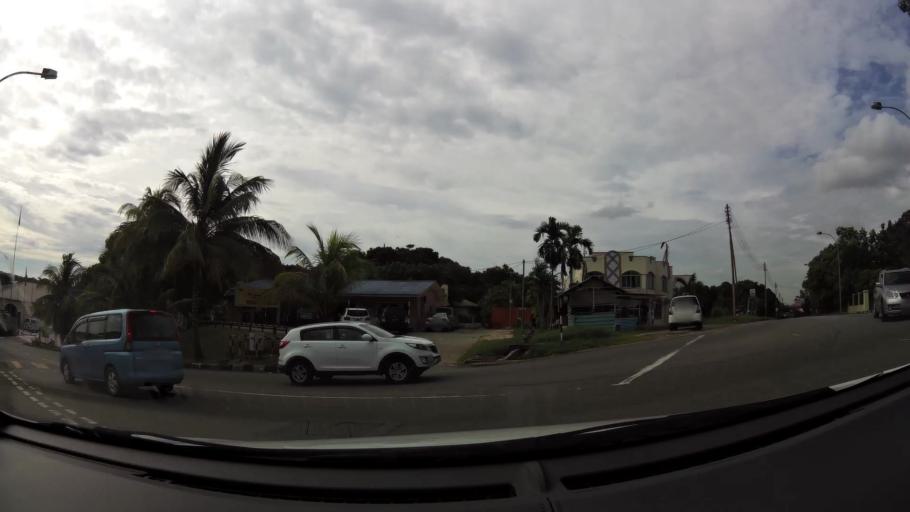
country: BN
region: Brunei and Muara
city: Bandar Seri Begawan
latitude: 4.8998
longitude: 114.8962
